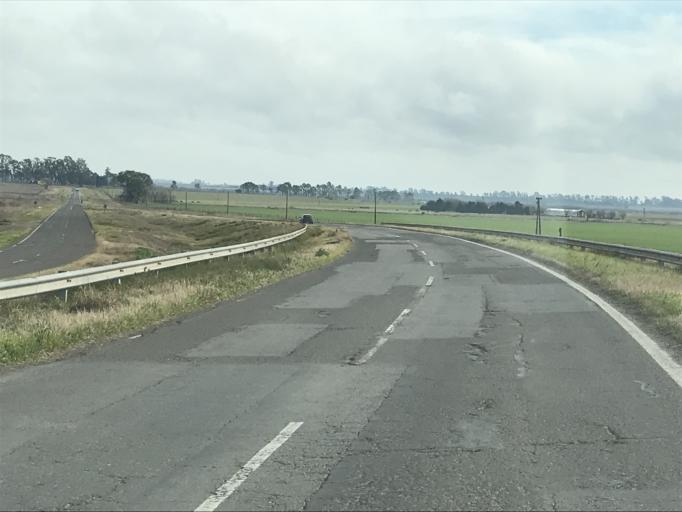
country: AR
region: Santa Fe
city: Carcarana
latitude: -32.8415
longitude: -61.2710
